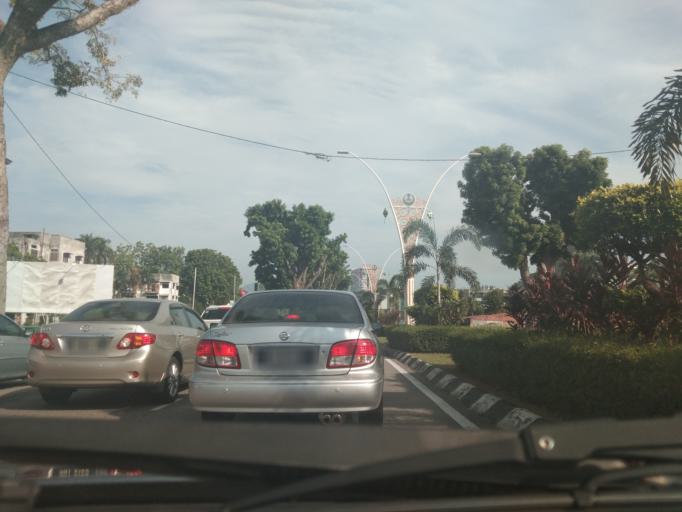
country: MY
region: Perak
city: Ipoh
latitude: 4.5908
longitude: 101.0916
